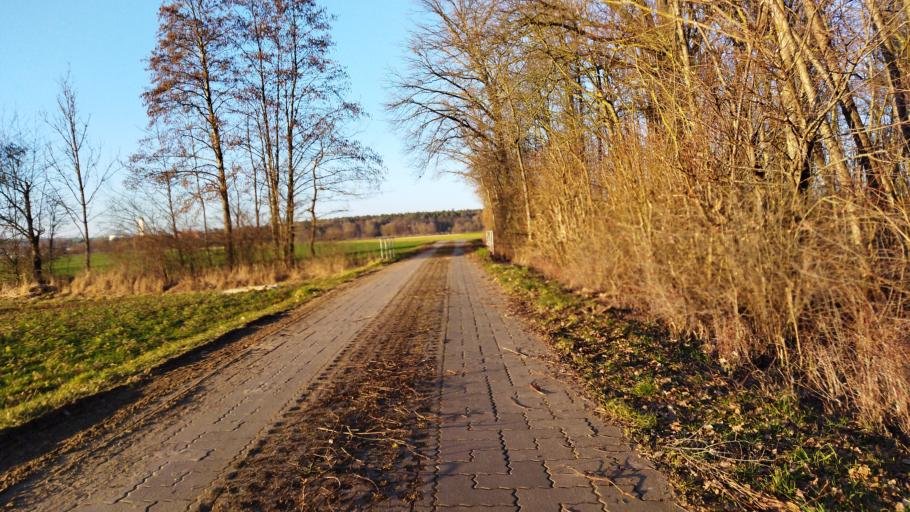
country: DE
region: Bavaria
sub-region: Regierungsbezirk Unterfranken
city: Dettelbach
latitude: 49.7863
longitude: 10.1987
